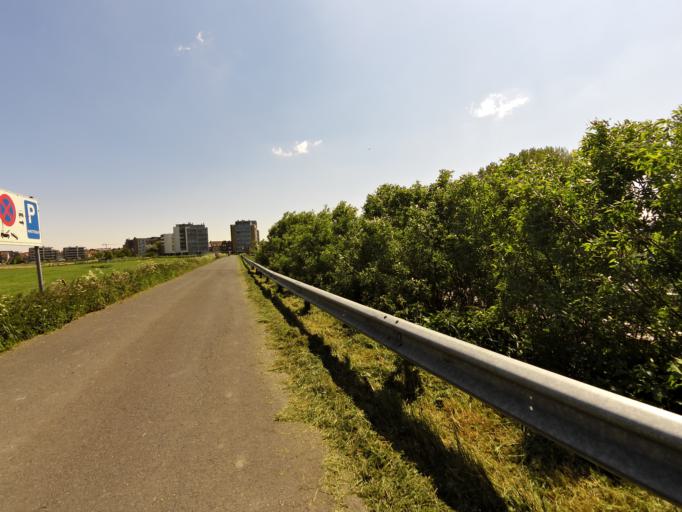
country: BE
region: Flanders
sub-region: Provincie West-Vlaanderen
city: Diksmuide
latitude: 51.0373
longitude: 2.8548
